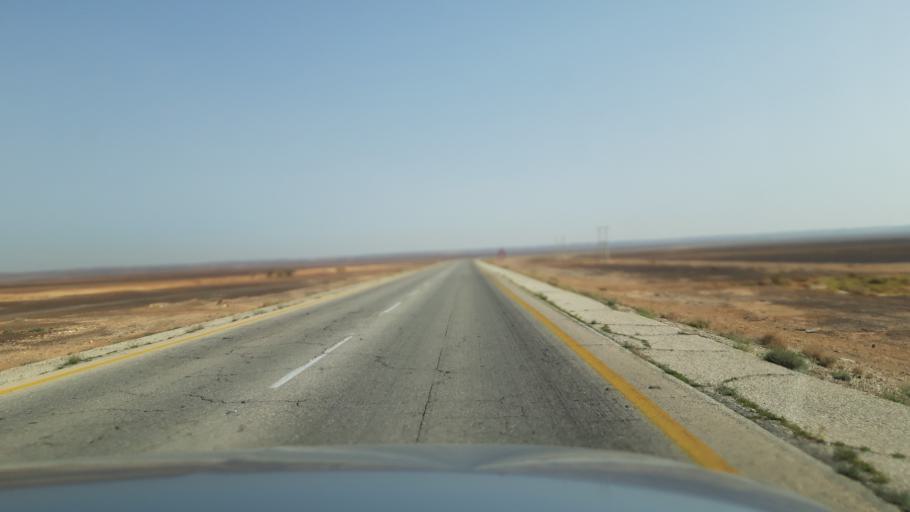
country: JO
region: Amman
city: Al Azraq ash Shamali
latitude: 31.8127
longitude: 36.5972
